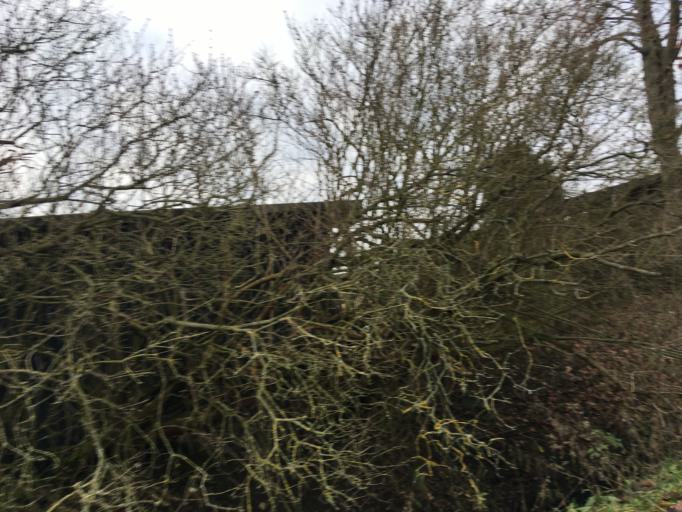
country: DE
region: Berlin
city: Niederschonhausen
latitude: 52.5789
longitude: 13.3867
